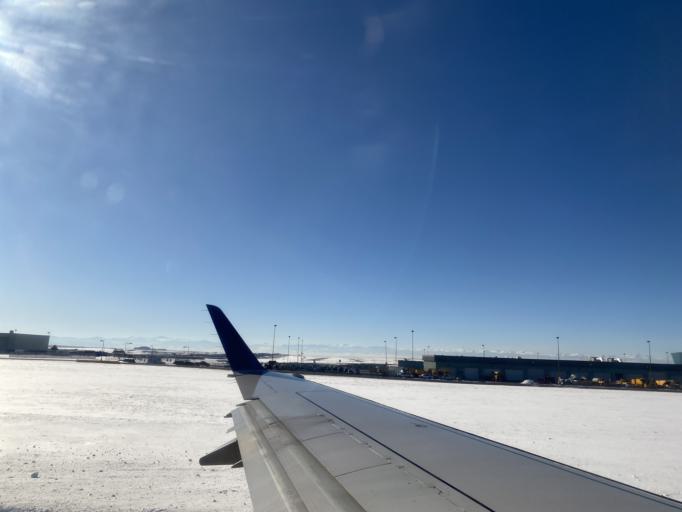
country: US
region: Colorado
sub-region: Weld County
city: Lochbuie
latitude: 39.8413
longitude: -104.6625
